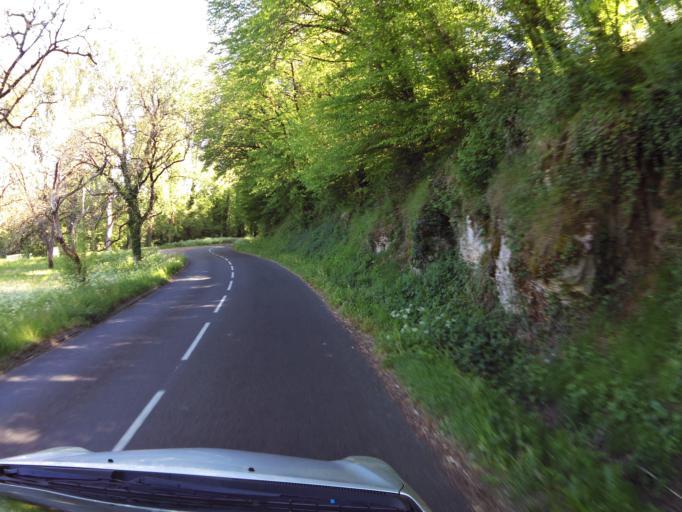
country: FR
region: Aquitaine
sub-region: Departement de la Dordogne
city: Carsac-Aillac
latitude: 44.8408
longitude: 1.3160
